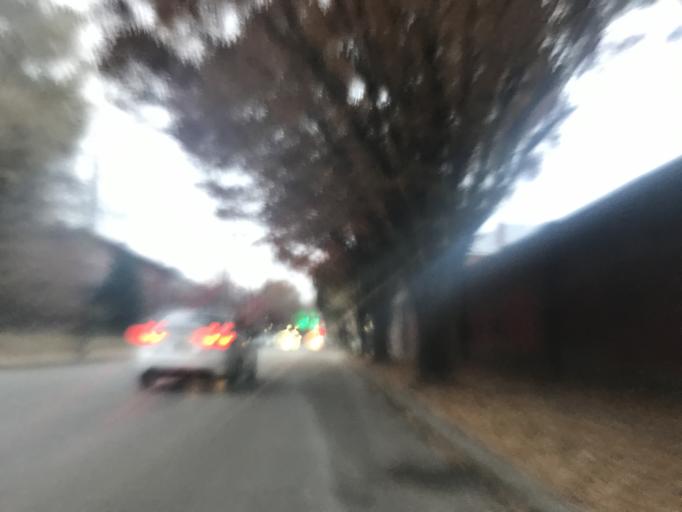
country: US
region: Kentucky
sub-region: Jefferson County
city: Louisville
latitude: 38.2321
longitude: -85.7642
